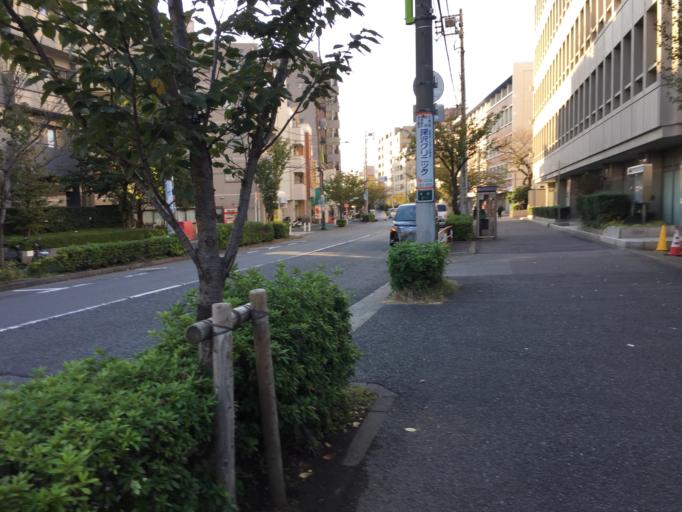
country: JP
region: Tokyo
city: Tokyo
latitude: 35.6312
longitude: 139.6505
